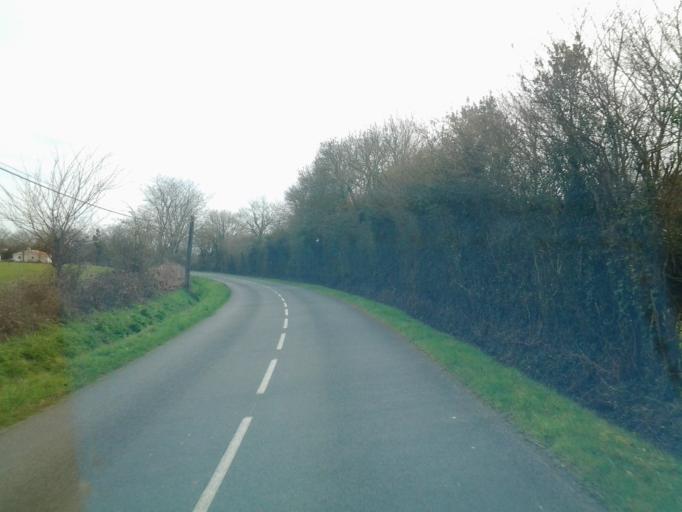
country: FR
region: Pays de la Loire
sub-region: Departement de la Vendee
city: Venansault
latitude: 46.6864
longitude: -1.5314
